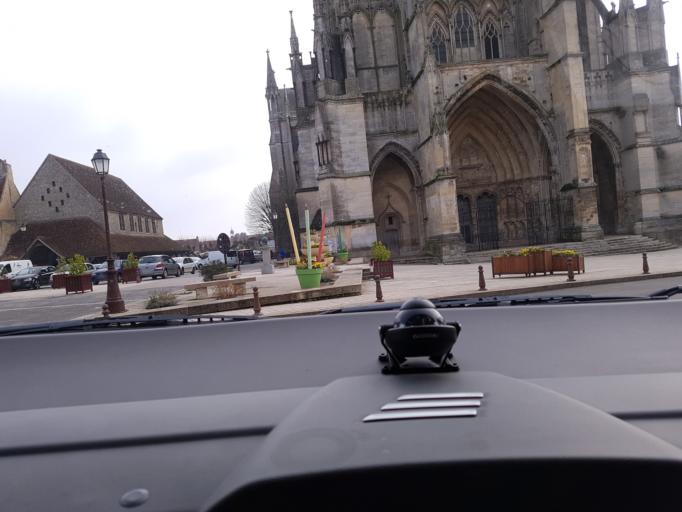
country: FR
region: Lower Normandy
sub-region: Departement de l'Orne
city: Sees
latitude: 48.6056
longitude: 0.1715
